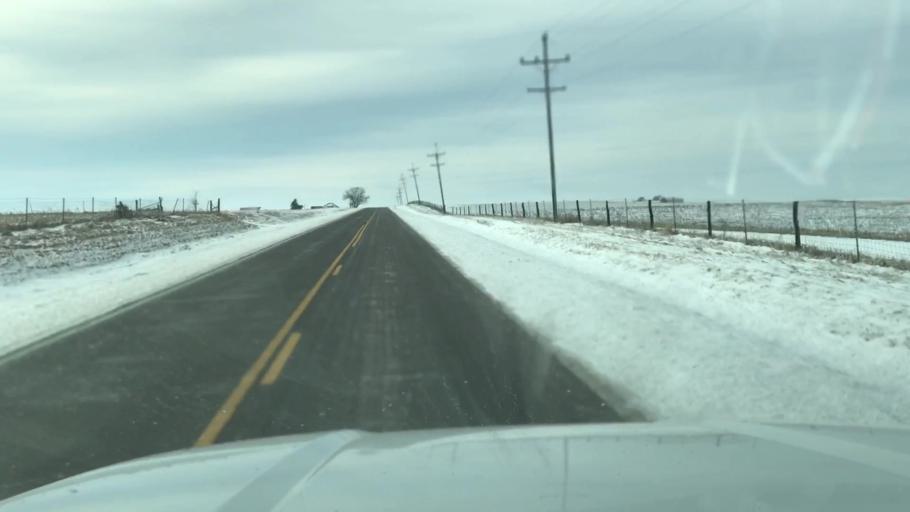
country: US
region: Missouri
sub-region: Holt County
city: Oregon
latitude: 40.0872
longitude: -95.1355
